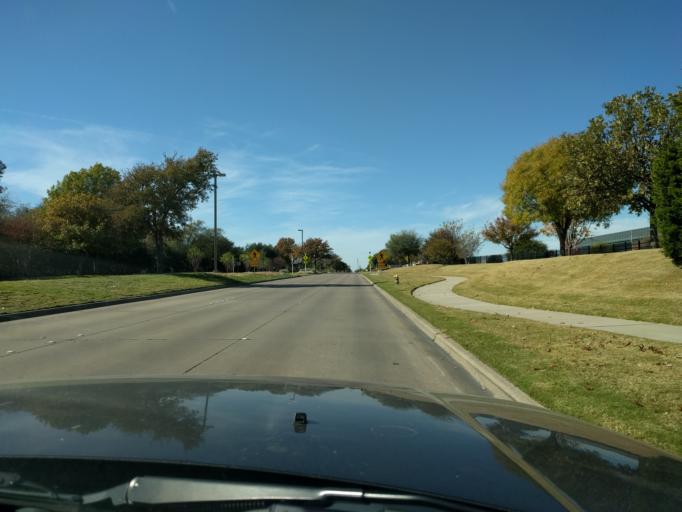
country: US
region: Texas
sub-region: Collin County
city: Plano
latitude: 32.9976
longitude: -96.7190
